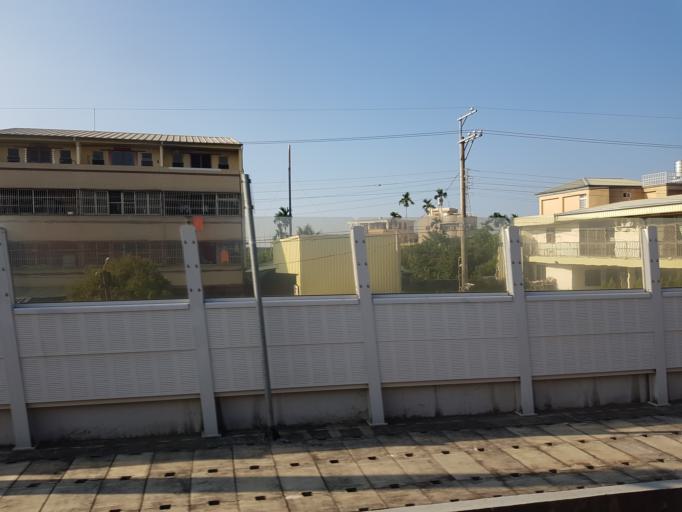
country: TW
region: Taiwan
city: Fengyuan
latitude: 24.2603
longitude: 120.7288
